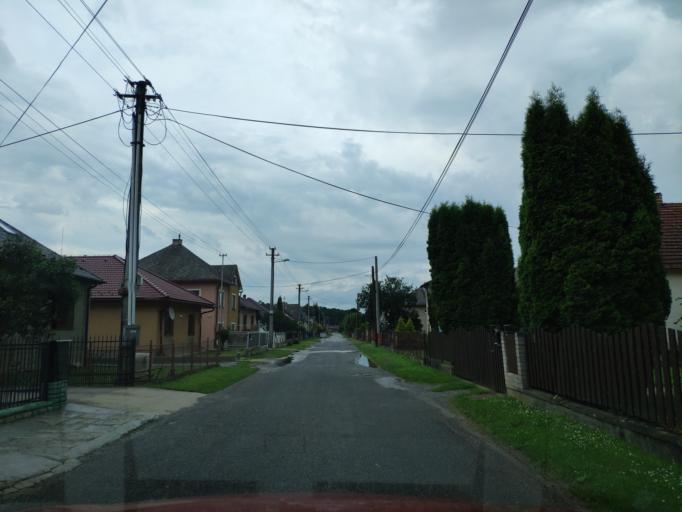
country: SK
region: Presovsky
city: Sabinov
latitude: 49.0034
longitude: 21.0867
